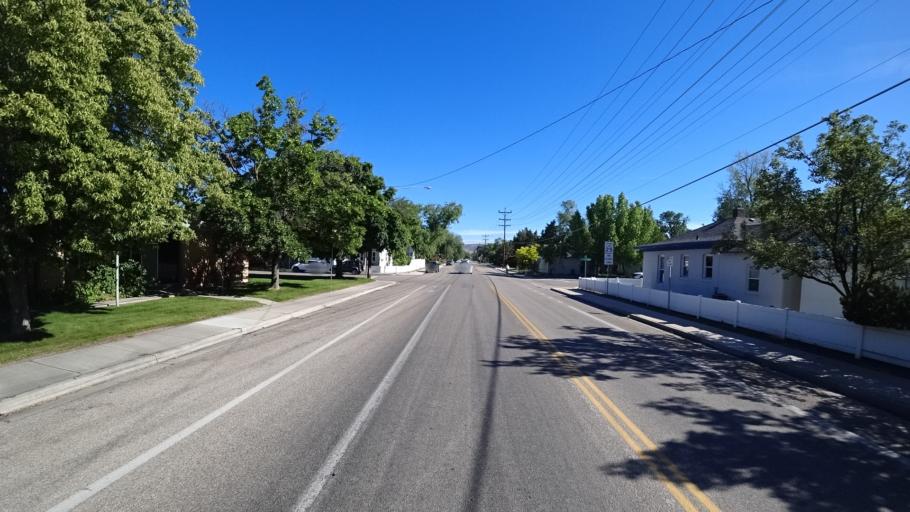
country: US
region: Idaho
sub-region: Ada County
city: Garden City
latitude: 43.6241
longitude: -116.2240
